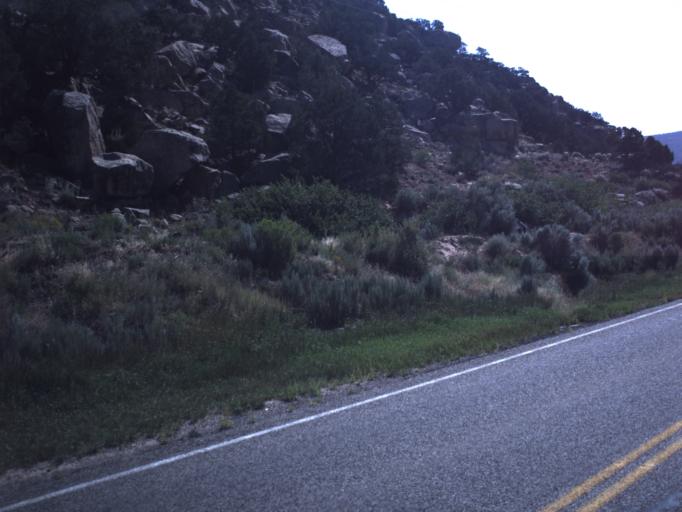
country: US
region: Utah
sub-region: Duchesne County
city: Duchesne
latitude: 40.3091
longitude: -110.6371
